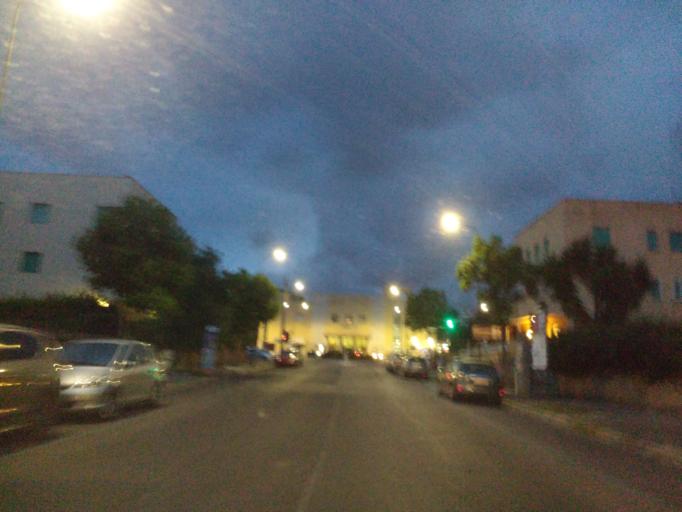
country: IT
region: Latium
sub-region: Citta metropolitana di Roma Capitale
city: Anzio
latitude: 41.4510
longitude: 12.6298
